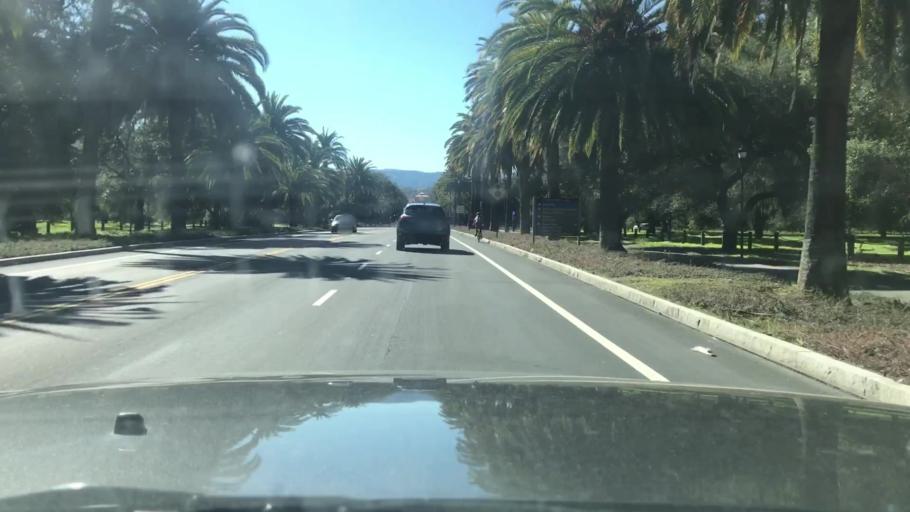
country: US
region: California
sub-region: Santa Clara County
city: Stanford
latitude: 37.4357
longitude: -122.1676
